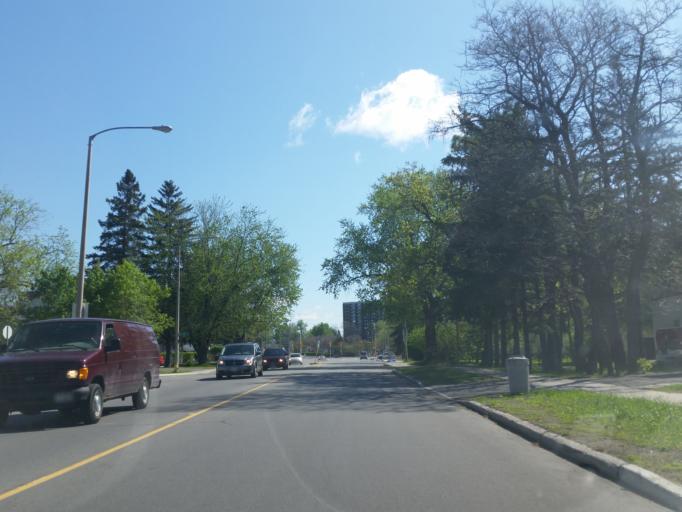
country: CA
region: Ontario
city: Ottawa
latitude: 45.3498
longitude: -75.7364
